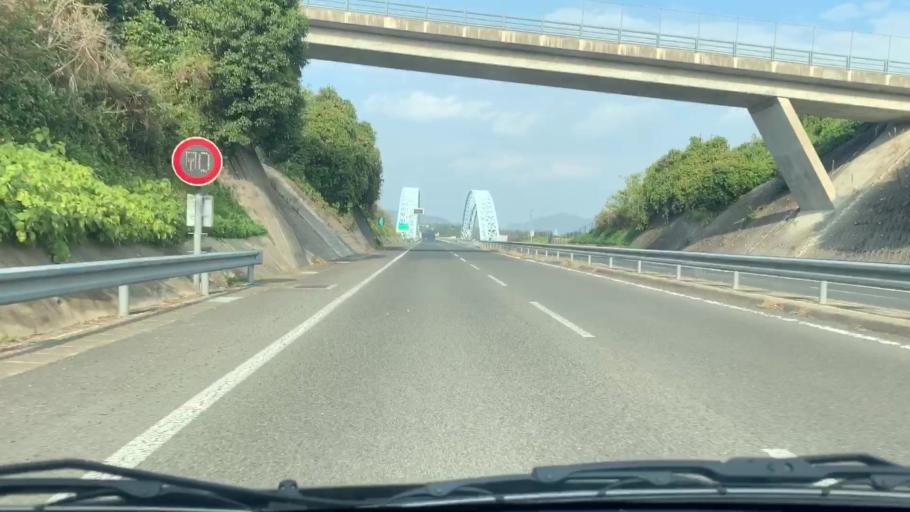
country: JP
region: Nagasaki
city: Sasebo
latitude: 33.0517
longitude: 129.7533
